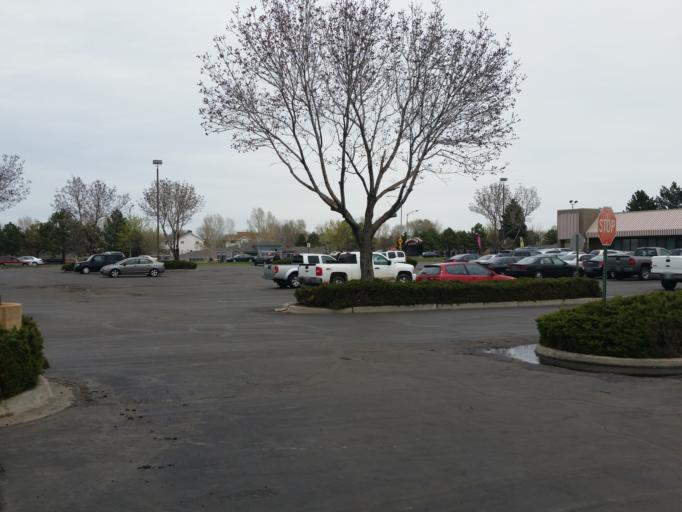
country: US
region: Colorado
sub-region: Adams County
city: Aurora
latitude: 39.6738
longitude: -104.8642
